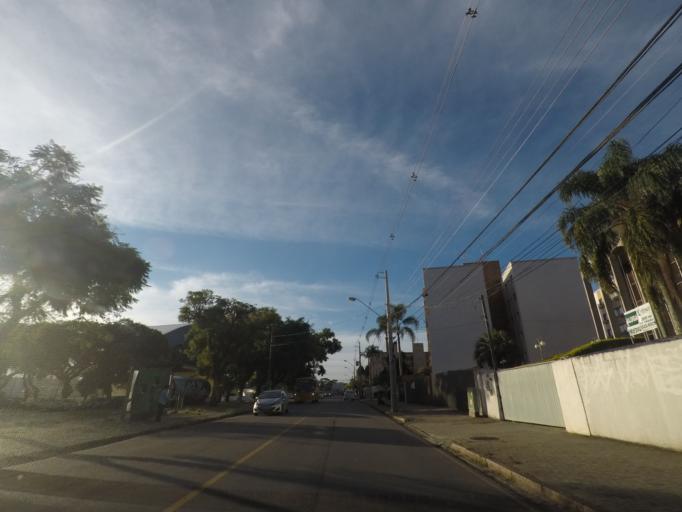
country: BR
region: Parana
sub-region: Curitiba
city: Curitiba
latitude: -25.4110
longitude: -49.2659
